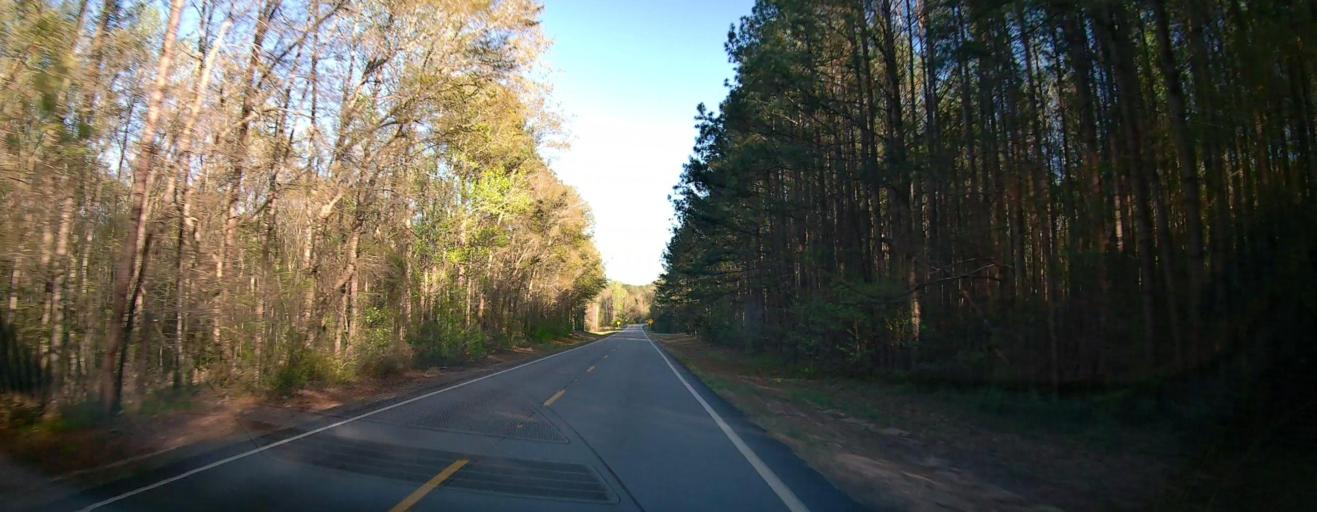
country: US
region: Georgia
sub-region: Wilkinson County
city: Irwinton
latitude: 32.9426
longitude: -83.1589
